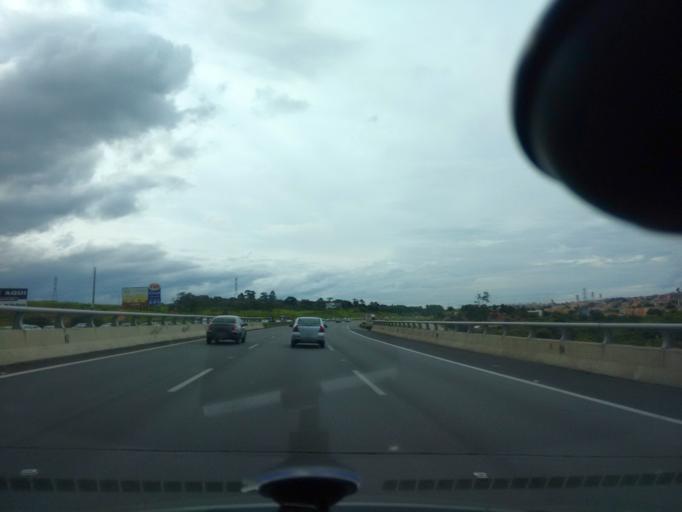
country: BR
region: Sao Paulo
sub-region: Campinas
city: Campinas
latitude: -22.9590
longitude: -47.1249
